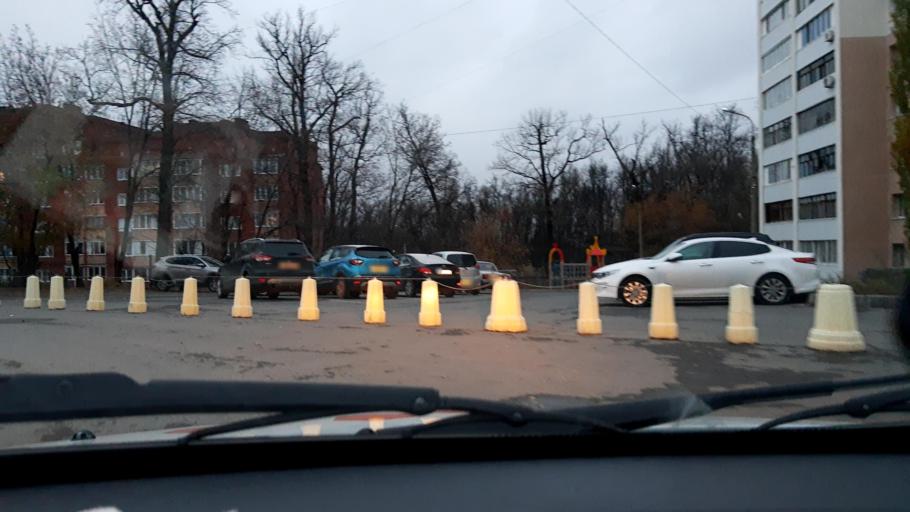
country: RU
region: Bashkortostan
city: Ufa
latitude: 54.7813
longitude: 56.0172
